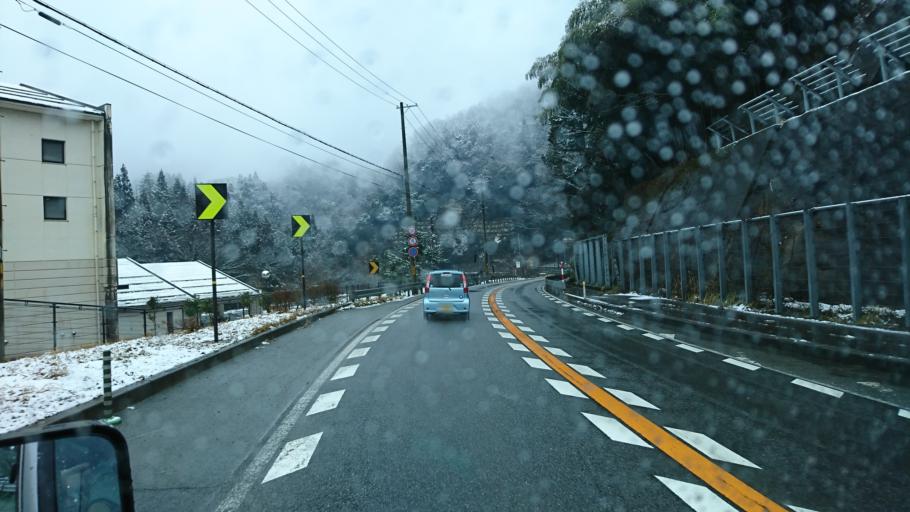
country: JP
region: Hyogo
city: Toyooka
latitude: 35.4784
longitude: 134.5852
